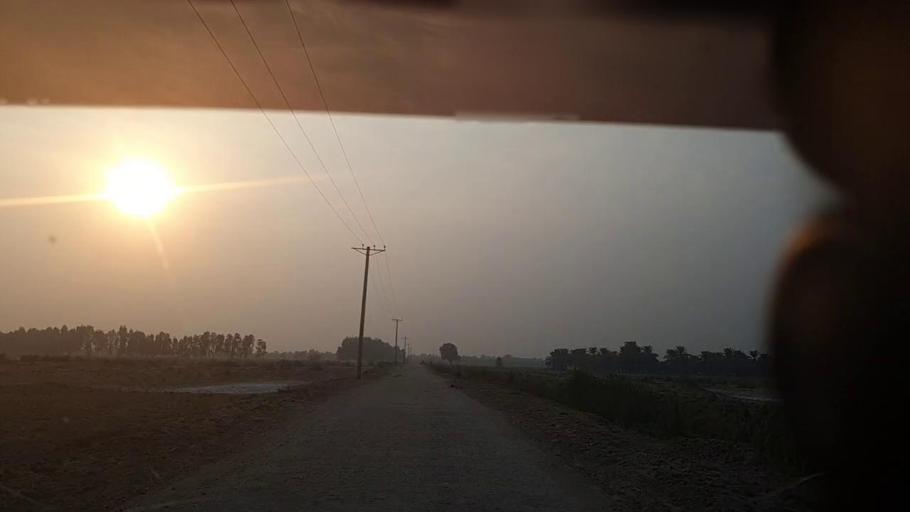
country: PK
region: Sindh
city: Pir jo Goth
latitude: 27.5277
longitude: 68.6724
